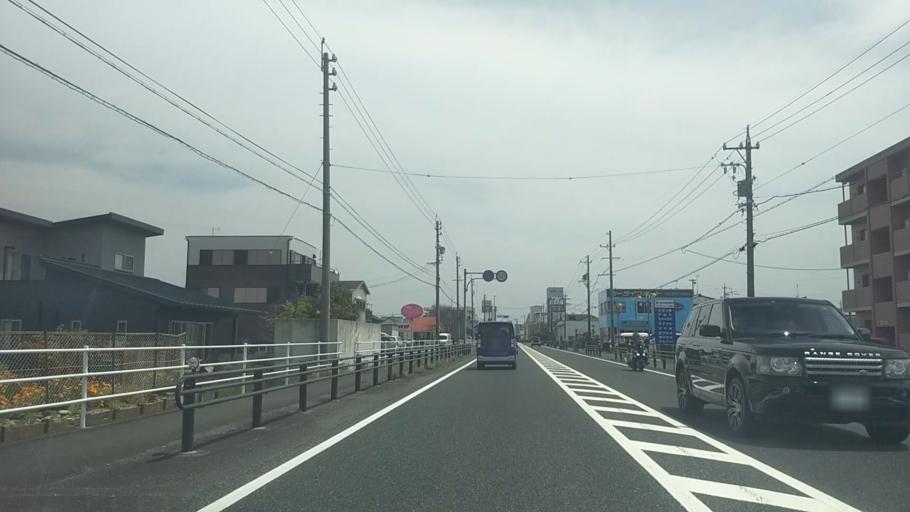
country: JP
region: Shizuoka
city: Kosai-shi
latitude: 34.6824
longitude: 137.6236
